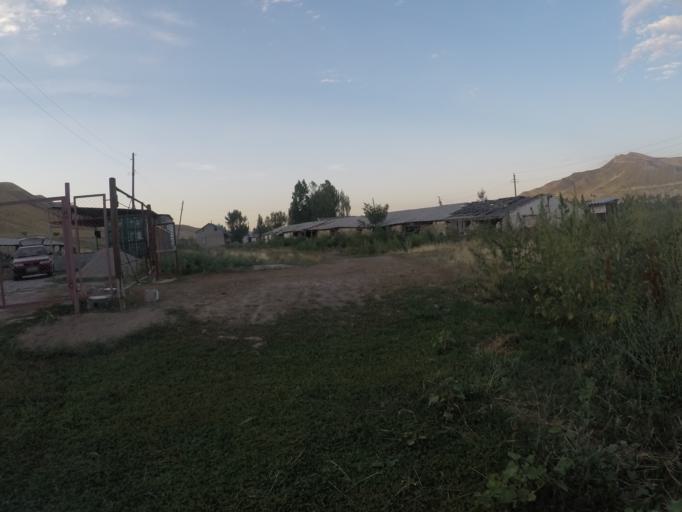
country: KG
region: Chuy
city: Bishkek
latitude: 42.7636
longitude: 74.6378
